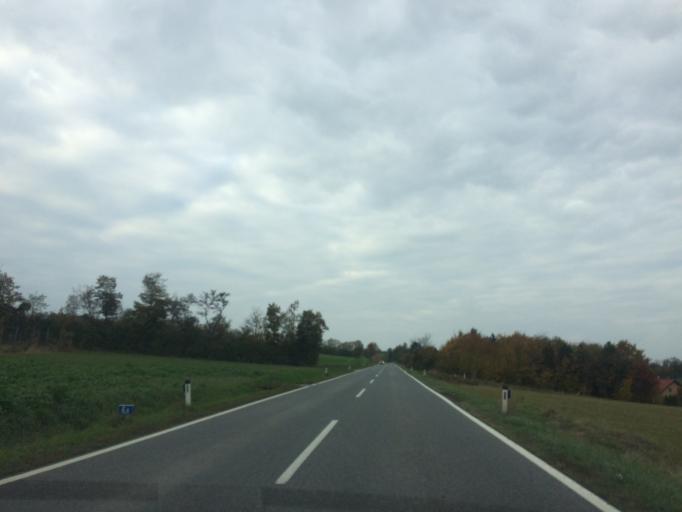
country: AT
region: Lower Austria
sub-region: Politischer Bezirk Tulln
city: Tulbing
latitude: 48.2662
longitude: 16.0757
